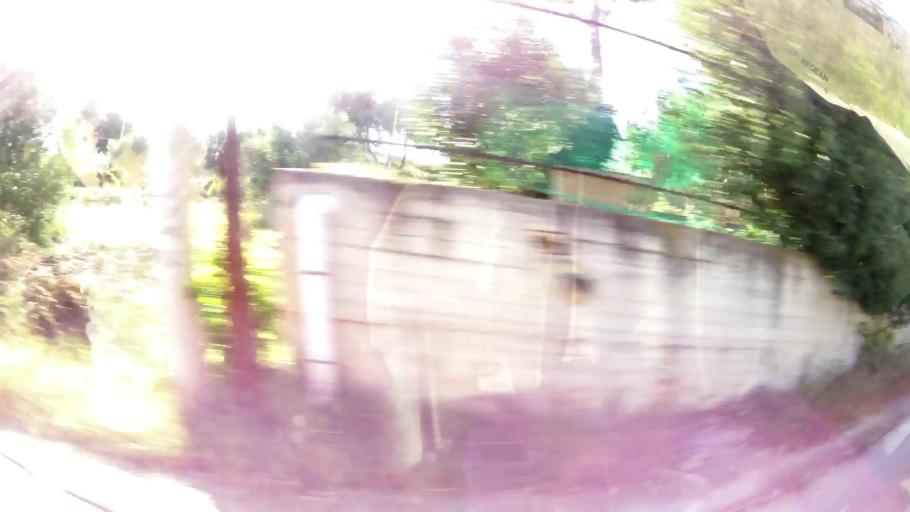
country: GR
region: Attica
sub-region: Nomarchia Anatolikis Attikis
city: Anthousa
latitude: 38.0197
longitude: 23.8679
